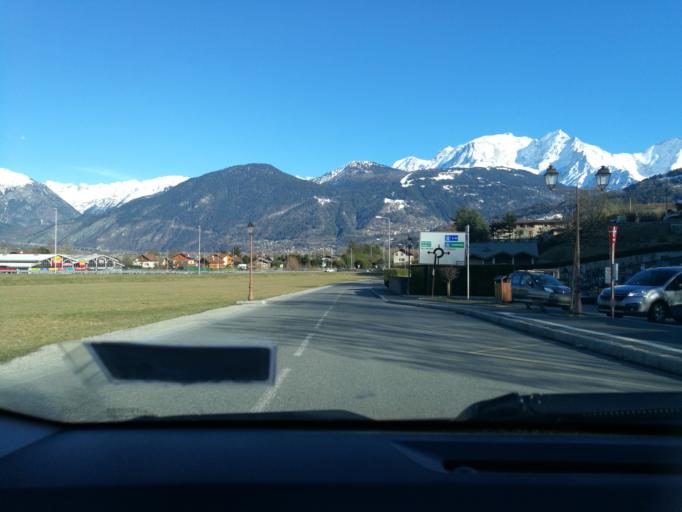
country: FR
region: Rhone-Alpes
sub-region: Departement de la Haute-Savoie
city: Domancy
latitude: 45.9104
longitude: 6.6549
